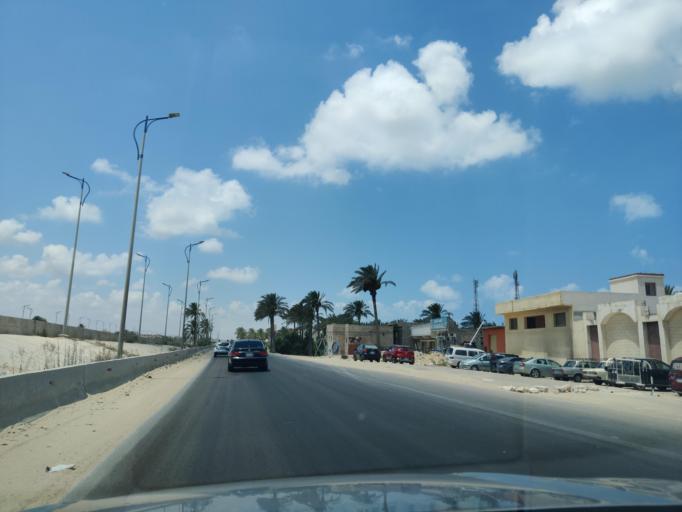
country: EG
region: Alexandria
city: Alexandria
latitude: 31.0072
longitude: 29.6202
